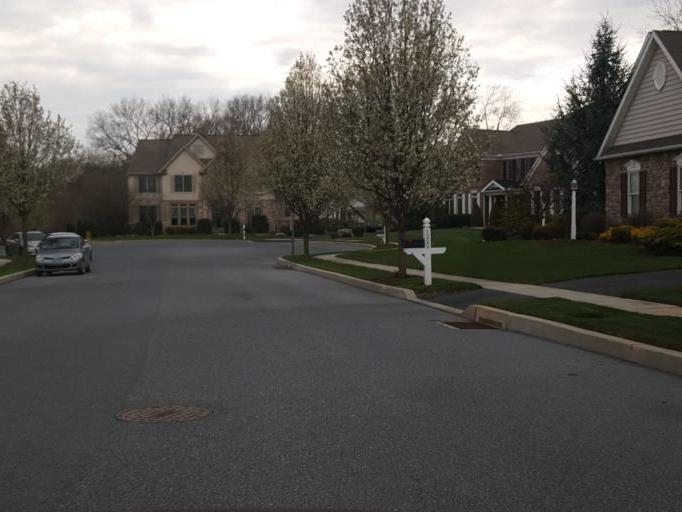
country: US
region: Pennsylvania
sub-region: Dauphin County
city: Hummelstown
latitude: 40.2378
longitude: -76.7226
